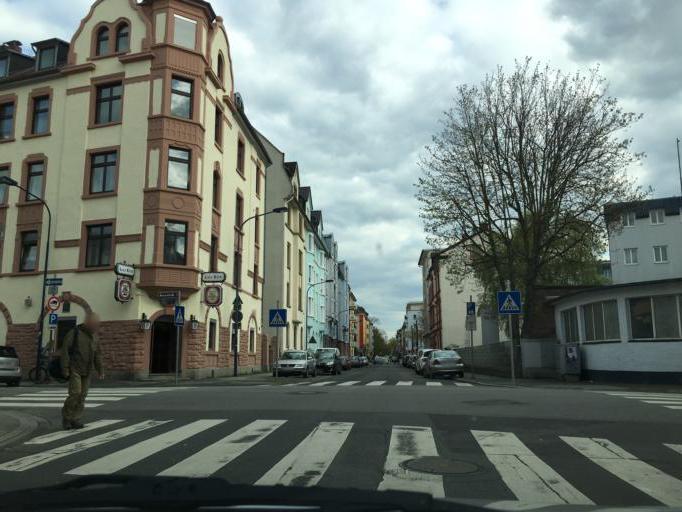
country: DE
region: Hesse
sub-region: Regierungsbezirk Darmstadt
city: Offenbach
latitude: 50.1079
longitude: 8.7486
